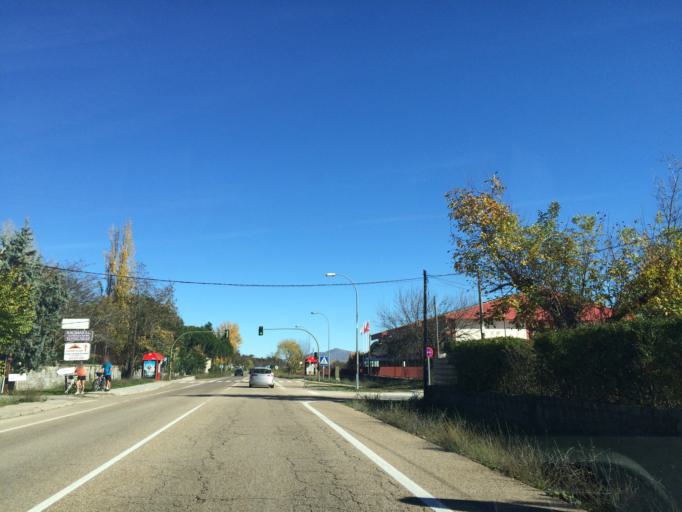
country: ES
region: Madrid
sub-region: Provincia de Madrid
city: Boalo
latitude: 40.7142
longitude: -3.9031
